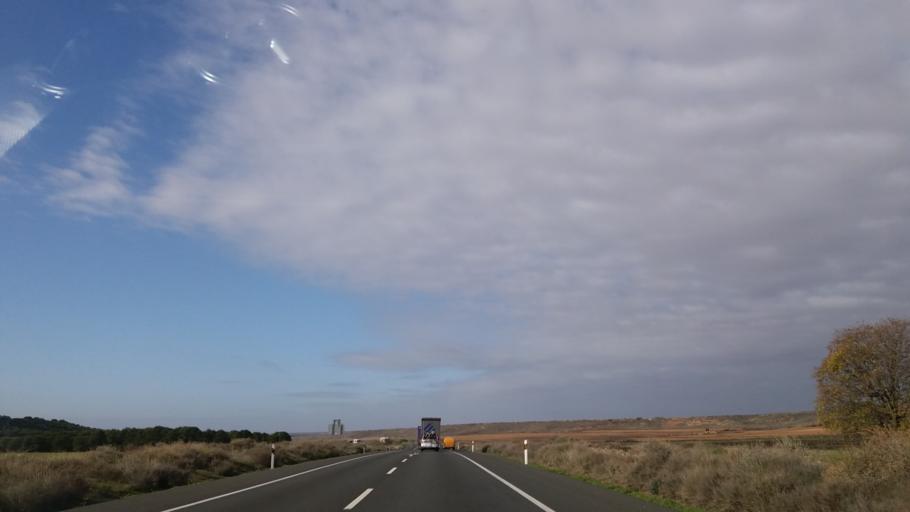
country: ES
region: Aragon
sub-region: Provincia de Huesca
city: Ballobar
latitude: 41.5208
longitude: 0.1970
